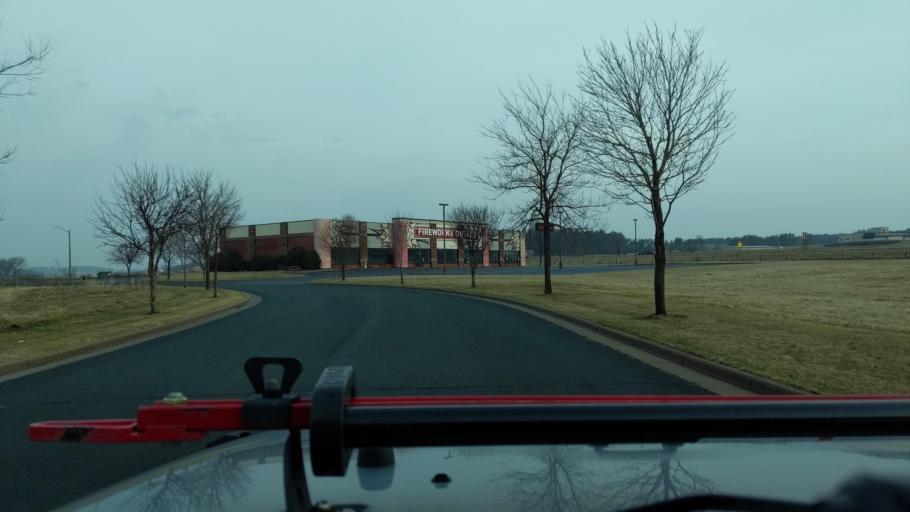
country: US
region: Wisconsin
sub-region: Saint Croix County
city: Baldwin
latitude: 44.9364
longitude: -92.3784
